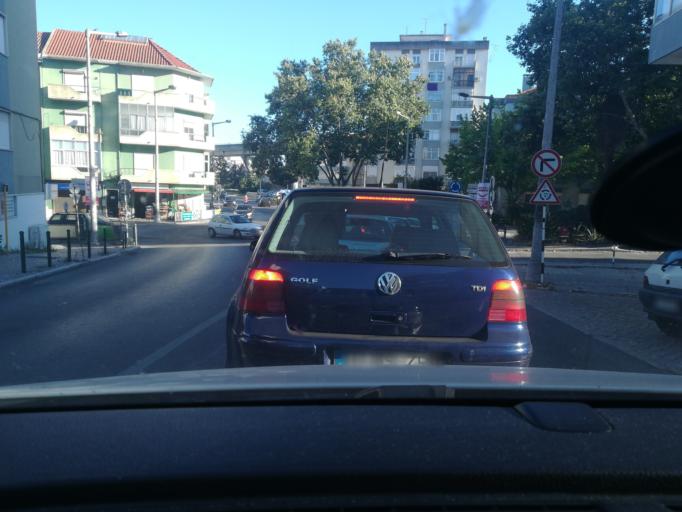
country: PT
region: Setubal
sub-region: Seixal
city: Corroios
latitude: 38.6419
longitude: -9.1572
